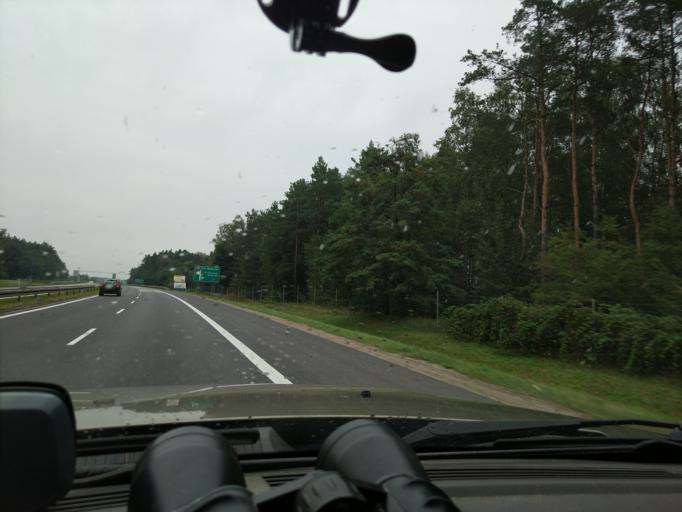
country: PL
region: Masovian Voivodeship
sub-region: Powiat ostrowski
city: Ostrow Mazowiecka
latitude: 52.7908
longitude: 21.8665
